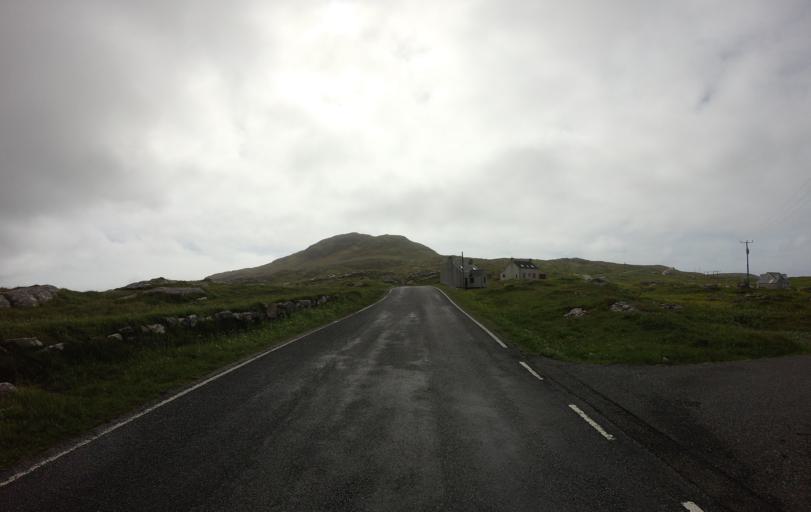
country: GB
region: Scotland
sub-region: Eilean Siar
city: Isle of South Uist
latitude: 57.0839
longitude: -7.3047
